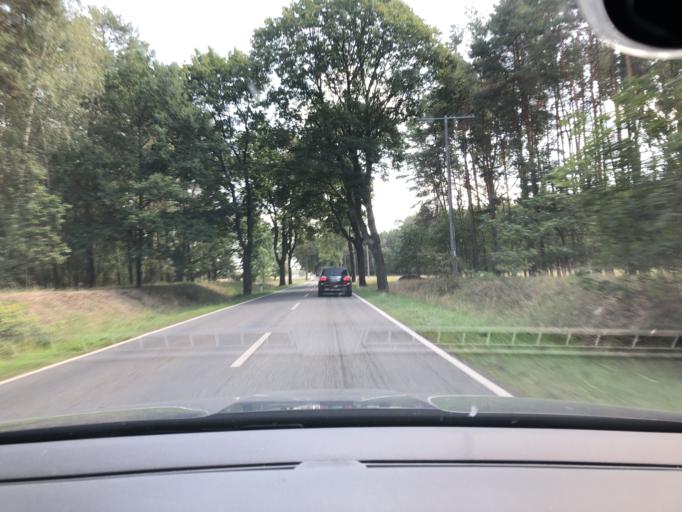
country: DE
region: Brandenburg
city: Ruthnick
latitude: 52.8923
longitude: 12.9851
